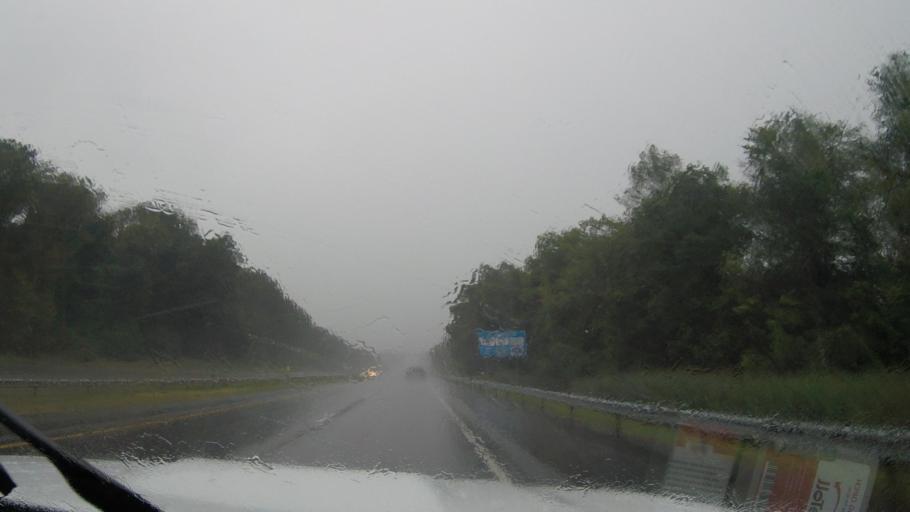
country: US
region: New York
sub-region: Ontario County
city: Phelps
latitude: 42.9550
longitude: -76.9979
